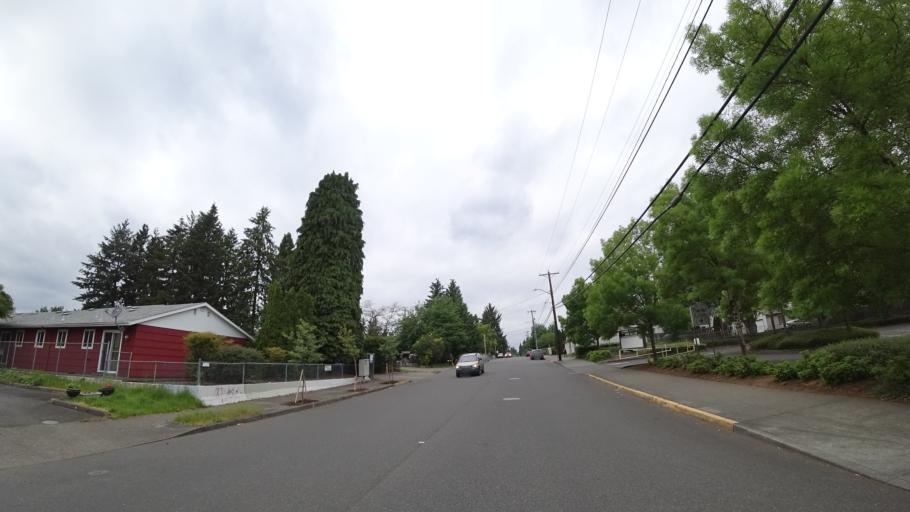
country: US
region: Oregon
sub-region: Multnomah County
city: Lents
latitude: 45.5135
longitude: -122.5300
